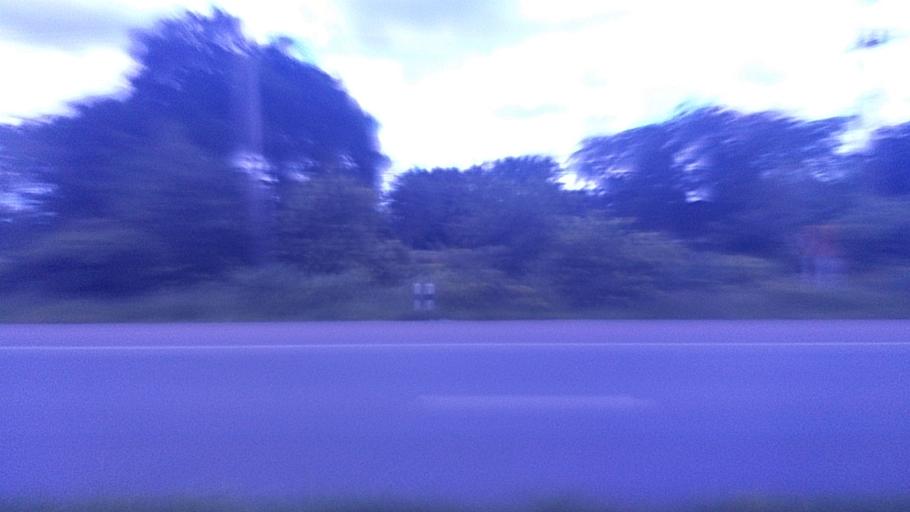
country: TH
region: Chaiyaphum
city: Chatturat
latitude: 15.6230
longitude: 101.9177
